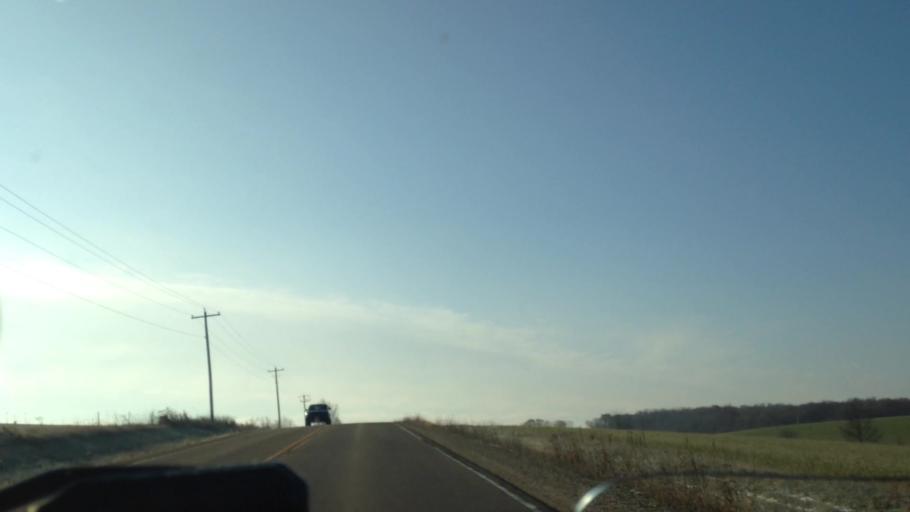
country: US
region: Wisconsin
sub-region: Dodge County
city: Mayville
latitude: 43.4602
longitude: -88.5000
